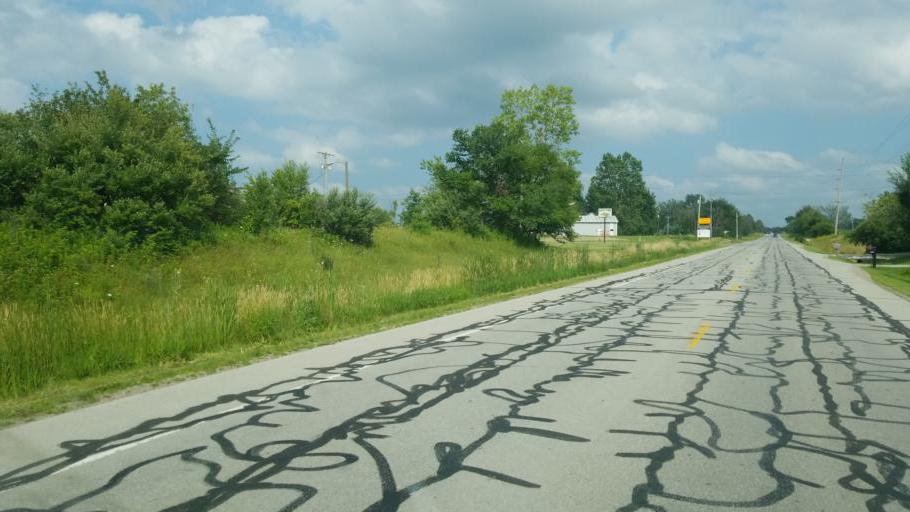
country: US
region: Ohio
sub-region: Crawford County
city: Crestline
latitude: 40.7848
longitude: -82.6831
